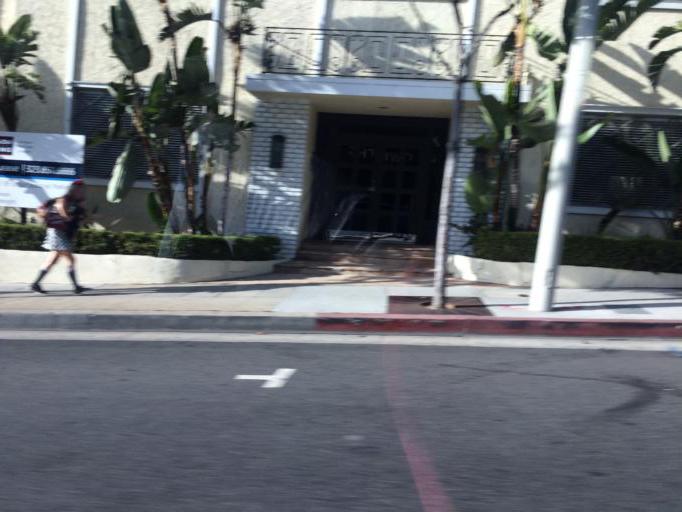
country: US
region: California
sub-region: Los Angeles County
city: West Hollywood
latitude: 34.0918
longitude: -118.3810
